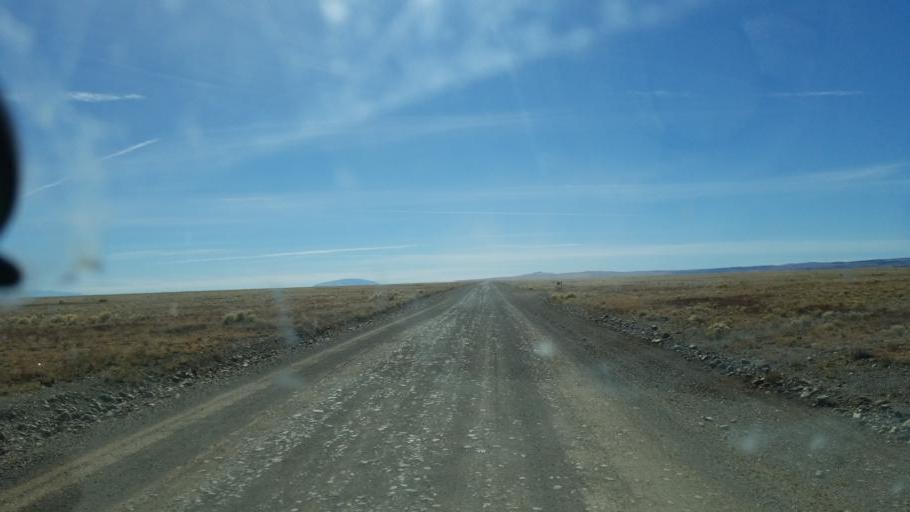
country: US
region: Colorado
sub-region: Rio Grande County
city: Monte Vista
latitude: 37.3587
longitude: -106.1492
